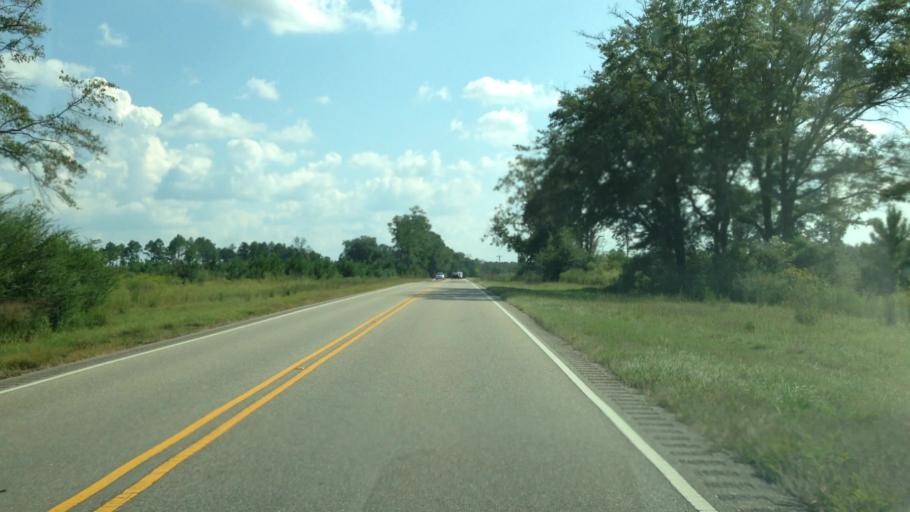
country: US
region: Alabama
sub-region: Covington County
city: Florala
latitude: 31.0696
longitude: -86.5750
